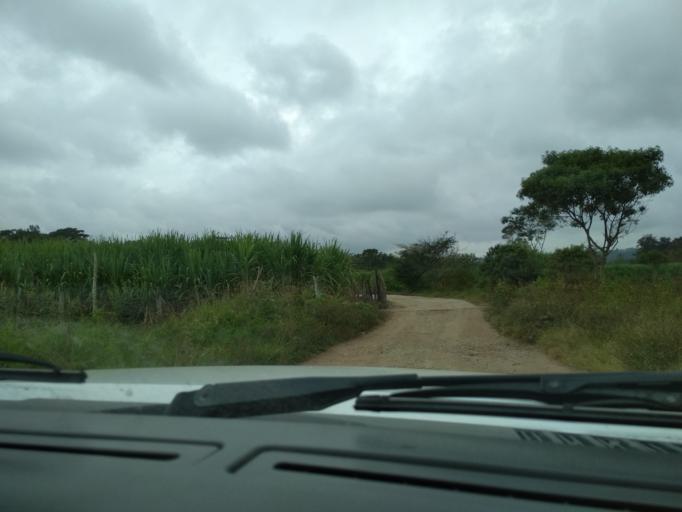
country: MX
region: Veracruz
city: El Castillo
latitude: 19.5433
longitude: -96.8504
